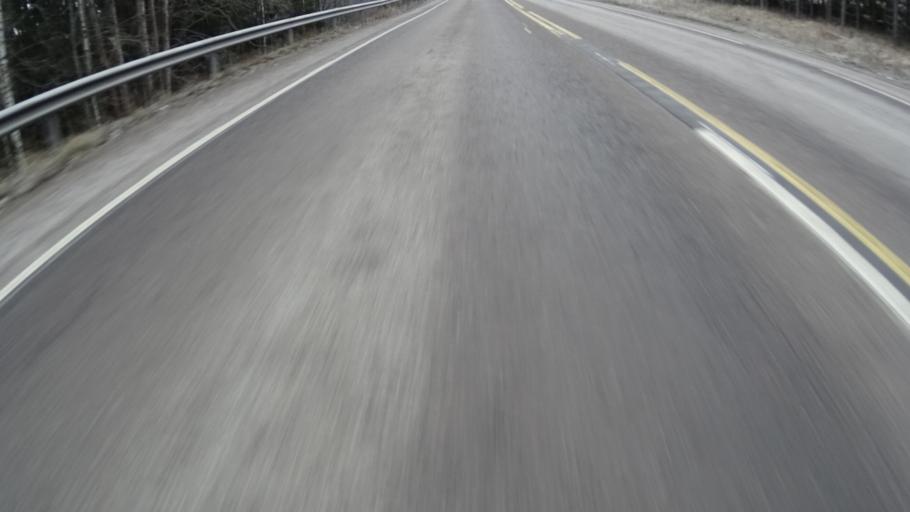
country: FI
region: Uusimaa
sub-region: Helsinki
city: Nurmijaervi
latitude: 60.4093
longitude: 24.7310
